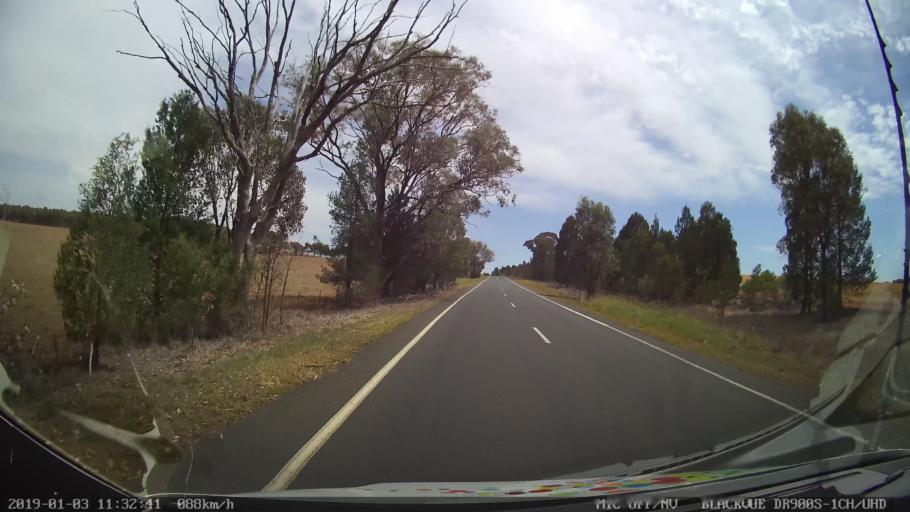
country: AU
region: New South Wales
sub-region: Weddin
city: Grenfell
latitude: -33.9553
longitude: 148.1770
